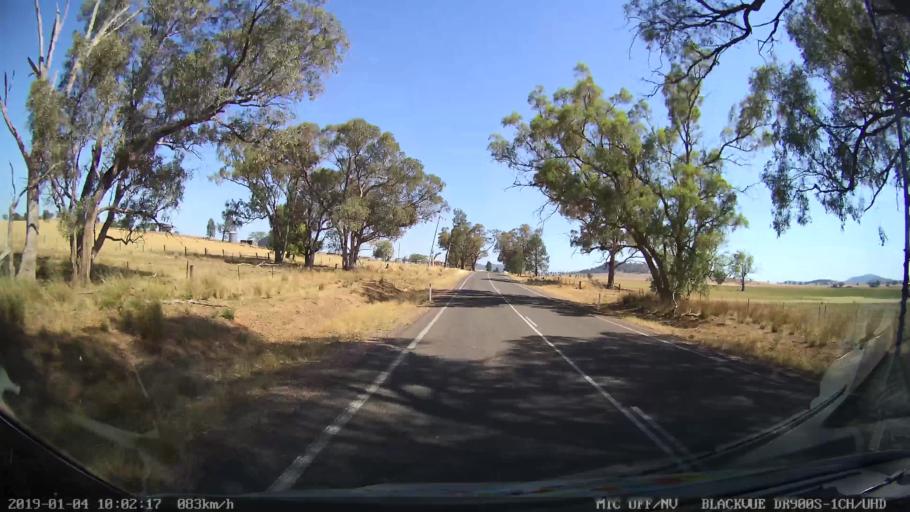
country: AU
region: New South Wales
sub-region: Cabonne
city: Canowindra
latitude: -33.4781
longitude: 148.3657
